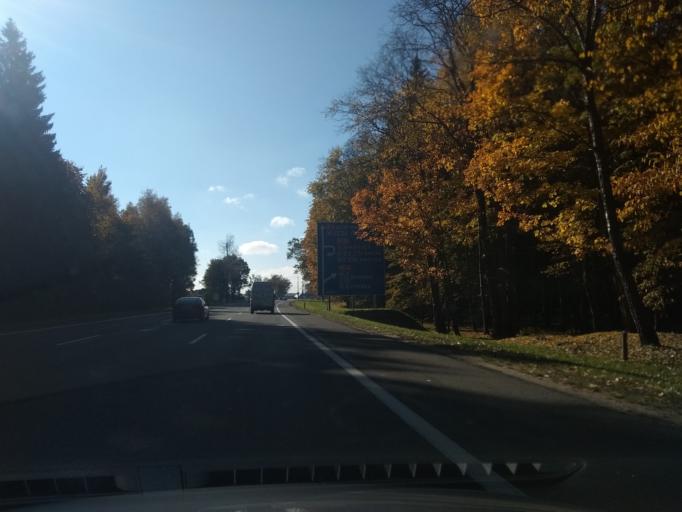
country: BY
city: Fanipol
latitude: 53.7839
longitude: 27.3633
